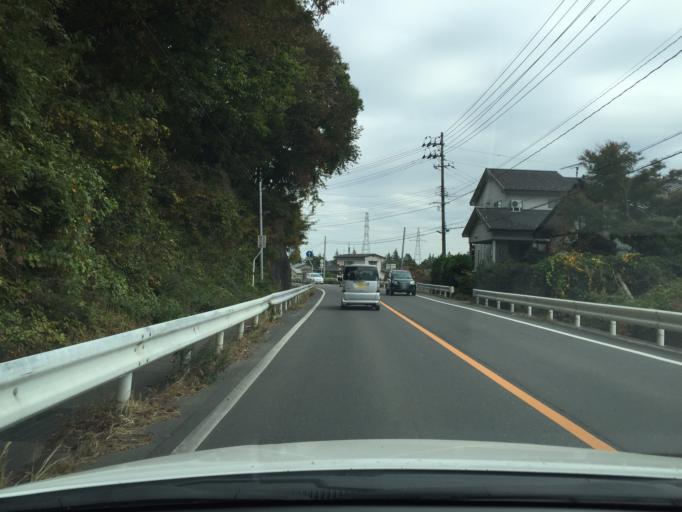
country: JP
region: Tochigi
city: Kuroiso
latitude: 37.1303
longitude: 140.1771
